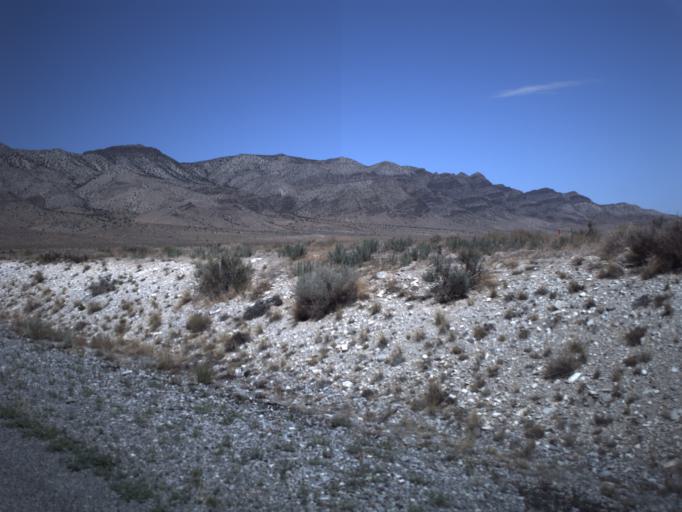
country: US
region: Utah
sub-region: Beaver County
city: Milford
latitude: 39.0860
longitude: -113.5276
